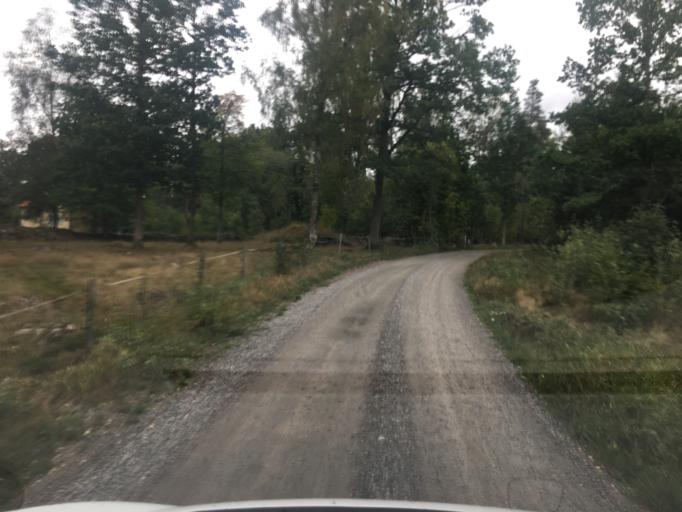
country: SE
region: Kronoberg
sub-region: Ljungby Kommun
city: Lagan
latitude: 56.9712
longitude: 14.0393
